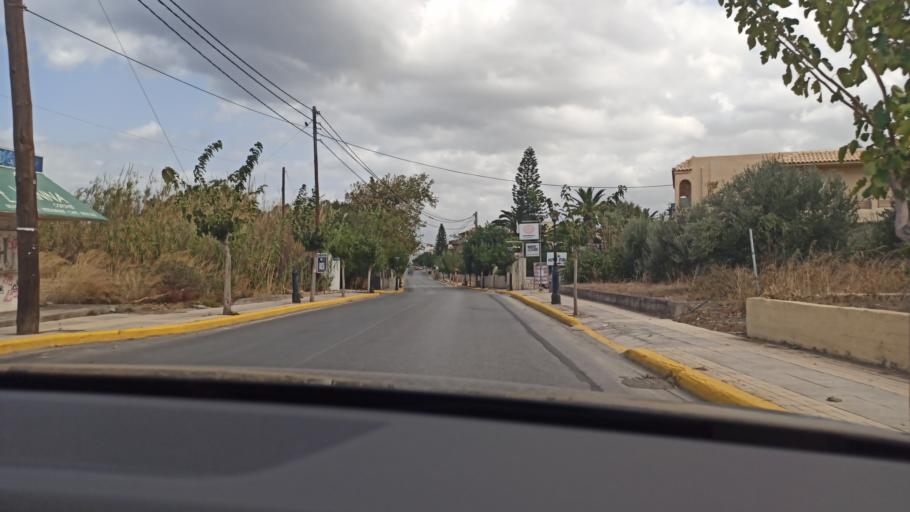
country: GR
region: Crete
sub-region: Nomos Irakleiou
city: Gazi
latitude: 35.3351
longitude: 25.0631
